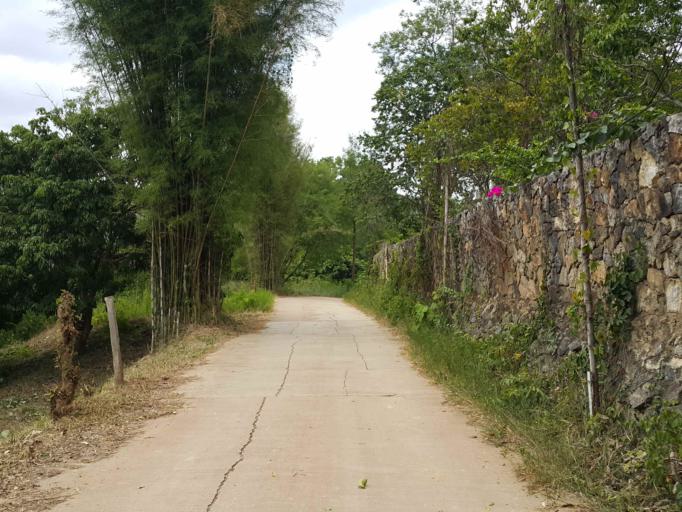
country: TH
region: Chiang Mai
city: Hang Dong
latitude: 18.7486
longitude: 98.8846
